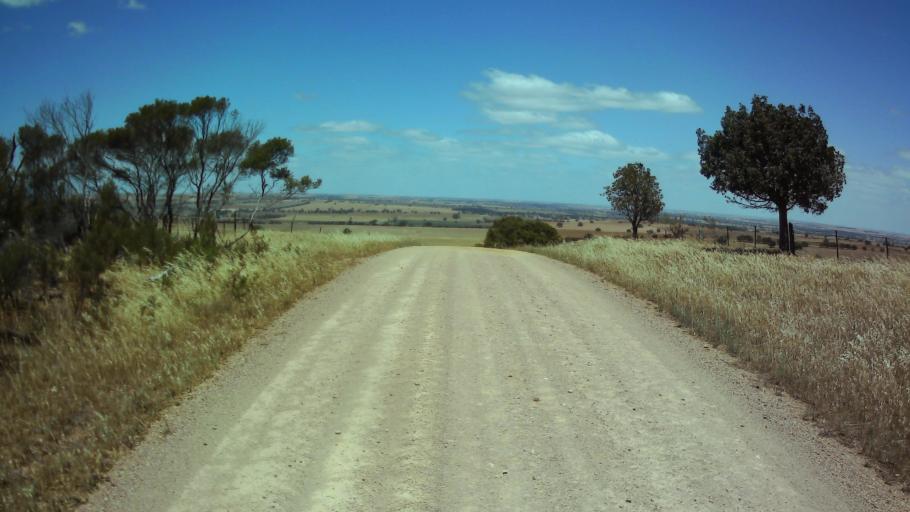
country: AU
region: New South Wales
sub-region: Weddin
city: Grenfell
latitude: -33.9575
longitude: 148.3652
